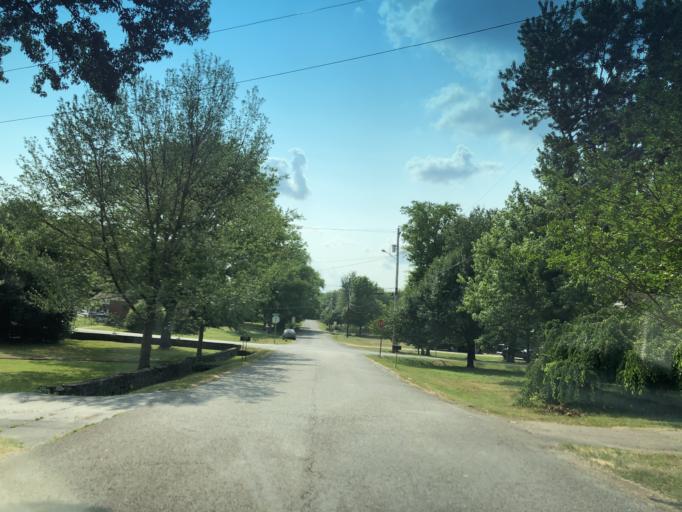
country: US
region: Tennessee
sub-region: Davidson County
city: Goodlettsville
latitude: 36.2647
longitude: -86.7187
